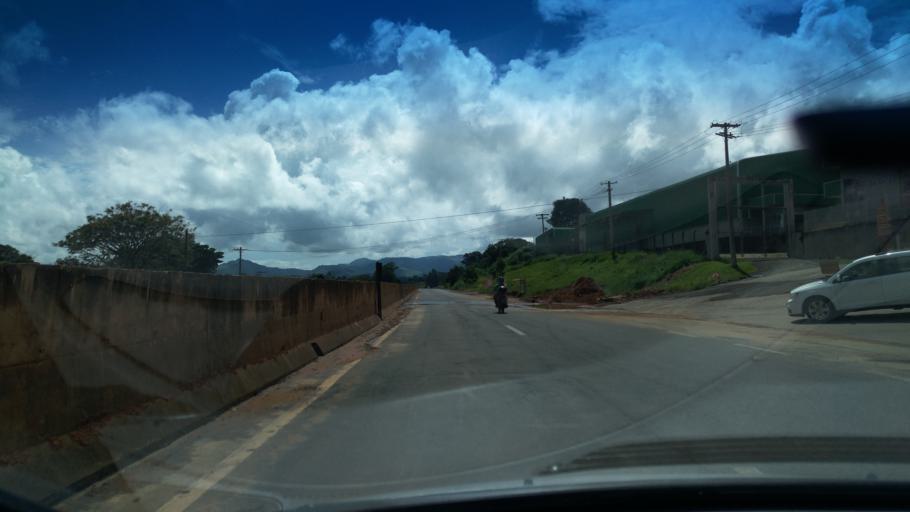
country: BR
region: Sao Paulo
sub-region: Santo Antonio Do Jardim
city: Espirito Santo do Pinhal
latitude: -22.1178
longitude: -46.6799
